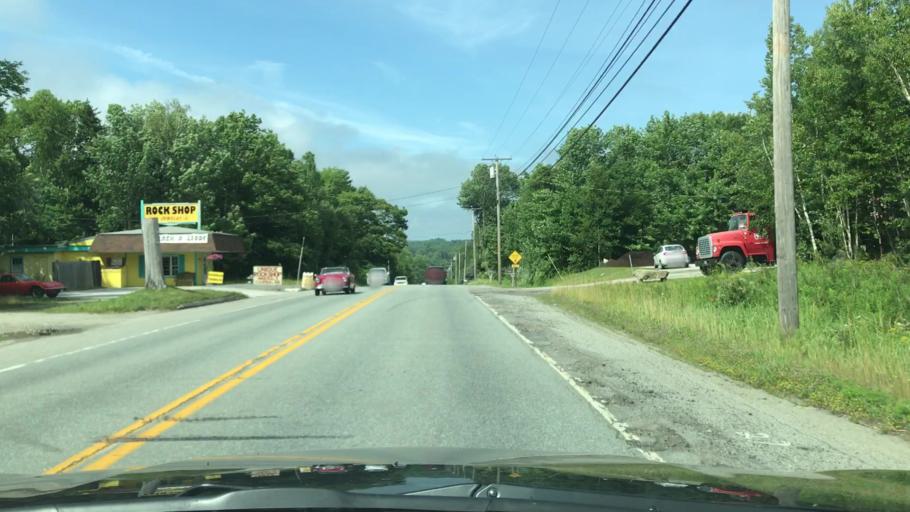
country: US
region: Maine
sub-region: Hancock County
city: Bucksport
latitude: 44.5599
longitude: -68.7928
